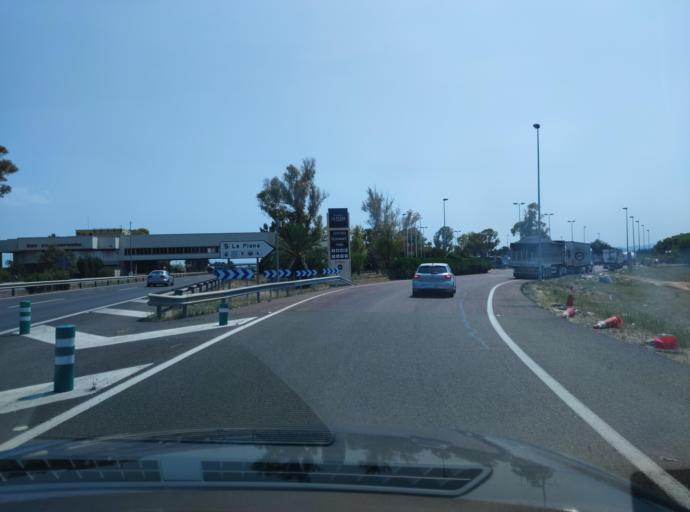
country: ES
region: Valencia
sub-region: Provincia de Castello
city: Alquerias del Nino Perdido
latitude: 39.8664
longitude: -0.1225
